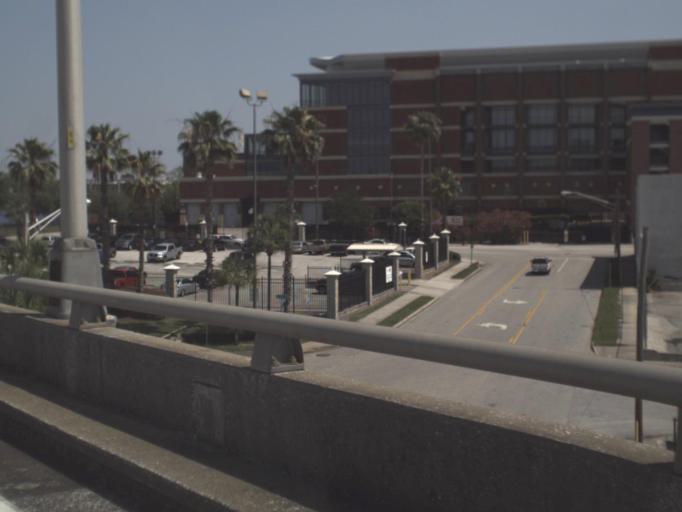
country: US
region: Florida
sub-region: Duval County
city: Jacksonville
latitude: 30.3236
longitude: -81.6455
